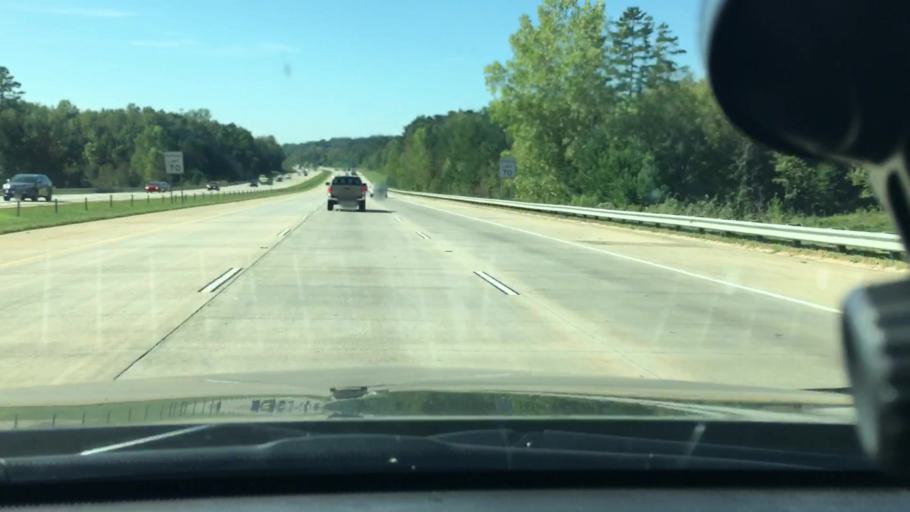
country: US
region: North Carolina
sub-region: Gaston County
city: Mount Holly
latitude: 35.3130
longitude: -80.9488
